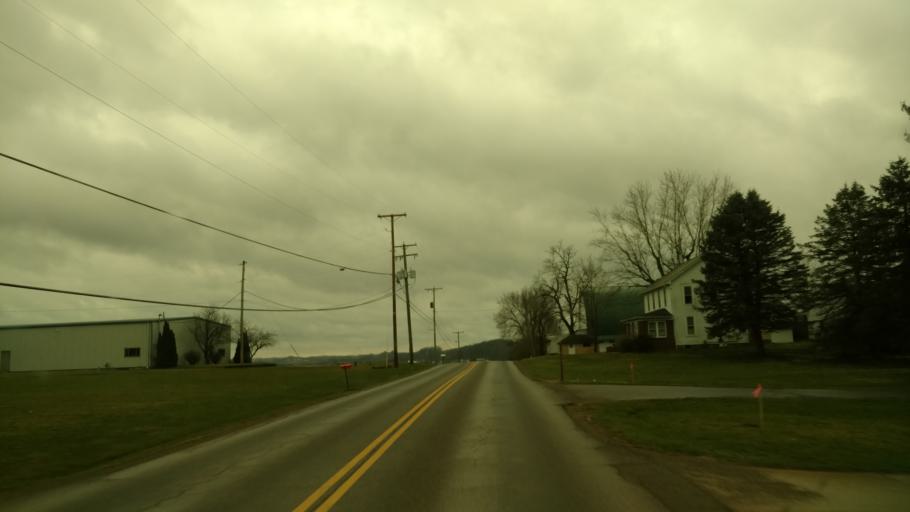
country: US
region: Ohio
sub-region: Holmes County
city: Millersburg
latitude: 40.5603
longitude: -81.8209
